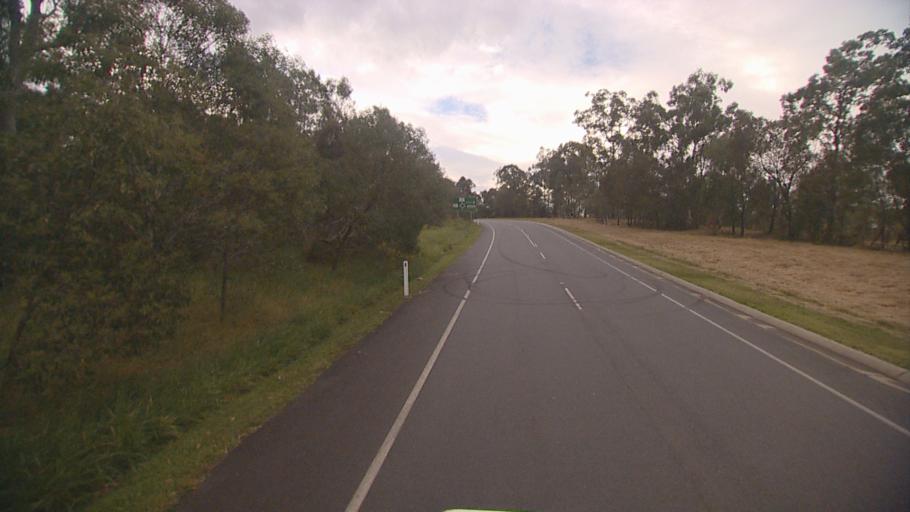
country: AU
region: Queensland
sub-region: Logan
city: Park Ridge South
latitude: -27.7281
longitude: 153.0291
